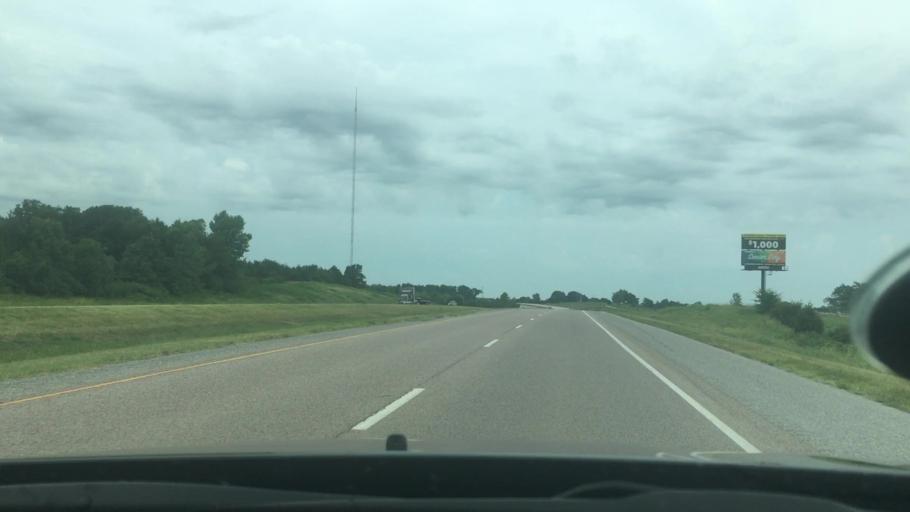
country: US
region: Oklahoma
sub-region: Pontotoc County
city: Byng
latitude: 34.8930
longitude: -96.6750
